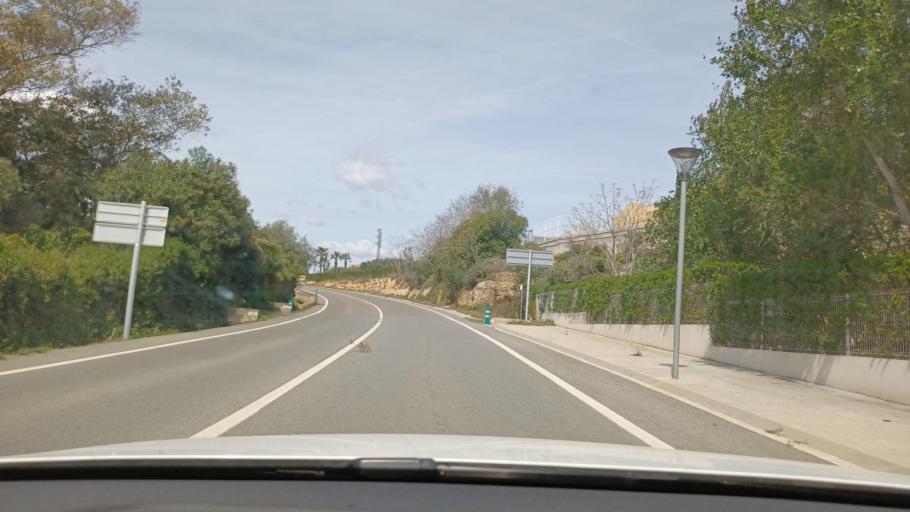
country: ES
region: Catalonia
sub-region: Provincia de Tarragona
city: L'Ampolla
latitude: 40.7996
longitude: 0.6954
